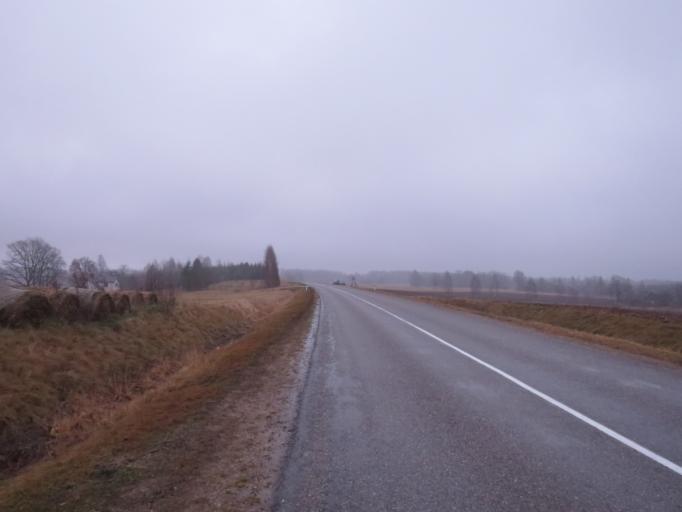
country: LV
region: Koknese
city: Koknese
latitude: 56.8805
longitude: 25.2926
